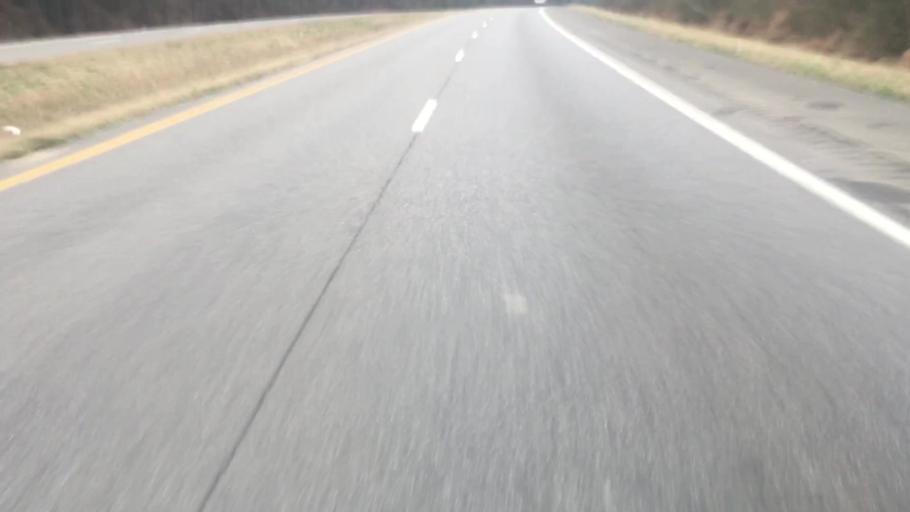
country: US
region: Alabama
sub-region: Jefferson County
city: Graysville
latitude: 33.6896
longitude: -86.9785
